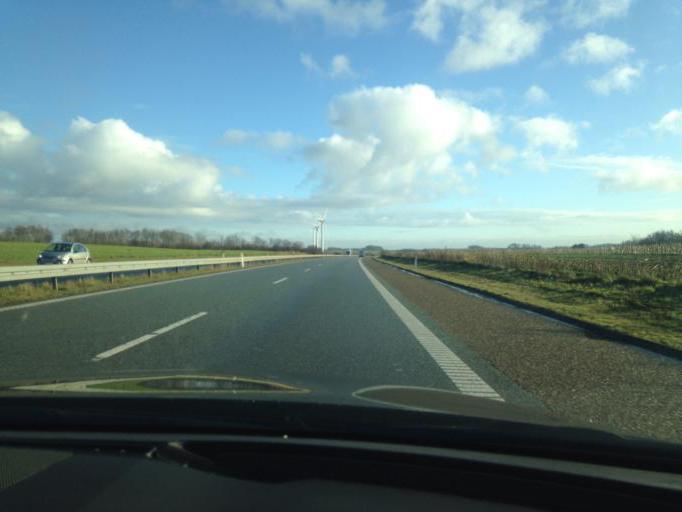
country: DK
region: South Denmark
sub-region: Vejen Kommune
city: Brorup
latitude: 55.5097
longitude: 8.9855
